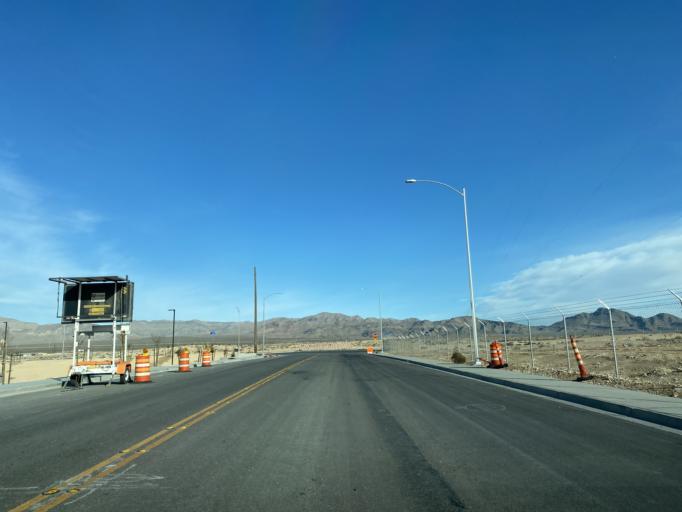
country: US
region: Nevada
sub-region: Clark County
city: Nellis Air Force Base
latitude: 36.2688
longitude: -115.0477
